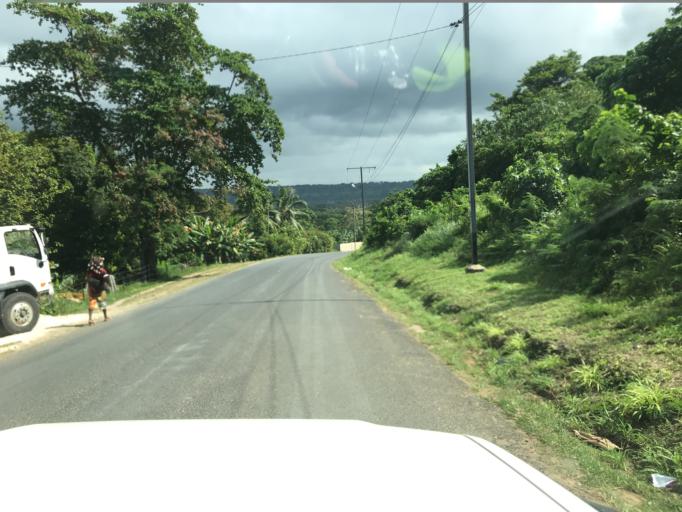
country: VU
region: Sanma
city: Luganville
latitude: -15.5105
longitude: 167.1802
